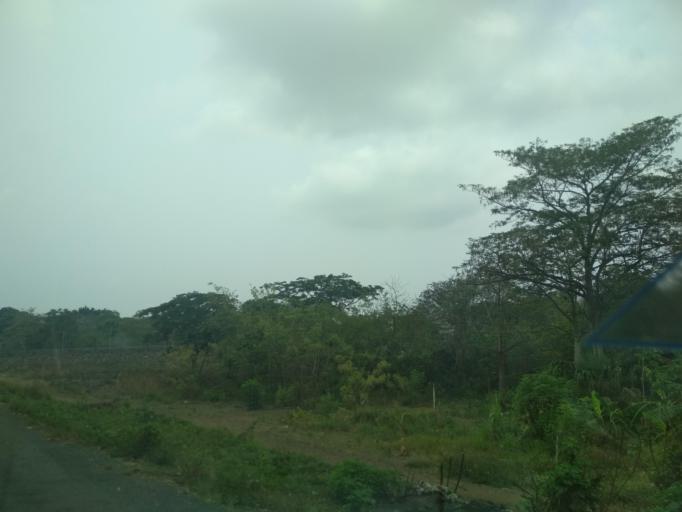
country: MX
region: Veracruz
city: Paso del Toro
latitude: 19.0245
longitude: -96.1365
